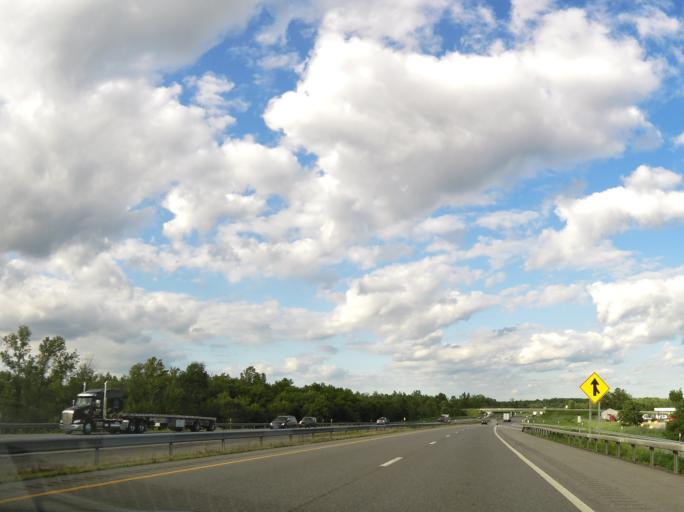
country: US
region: New York
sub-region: Erie County
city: Akron
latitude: 43.0047
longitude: -78.4104
